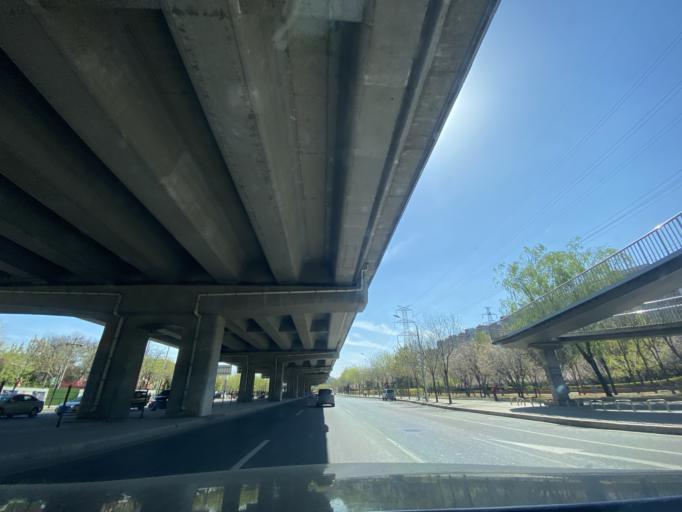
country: CN
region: Beijing
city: Babaoshan
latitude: 39.9241
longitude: 116.2478
